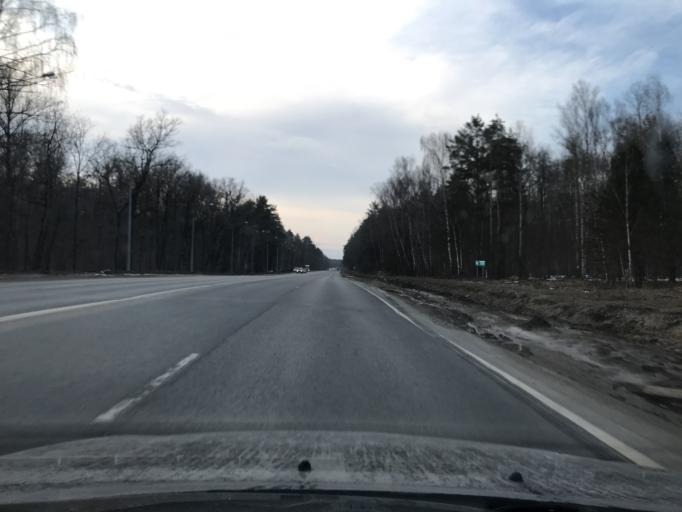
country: RU
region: Kaluga
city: Mstikhino
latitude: 54.5891
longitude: 36.0657
